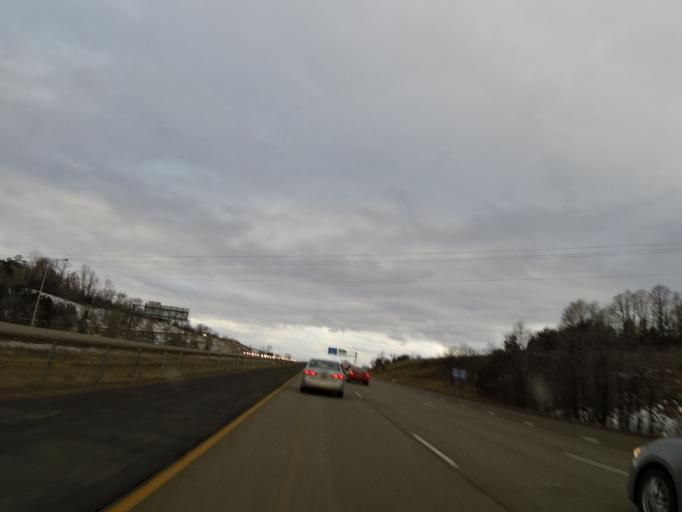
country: US
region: Minnesota
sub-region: Washington County
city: Lakeland
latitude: 44.9607
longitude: -92.7782
